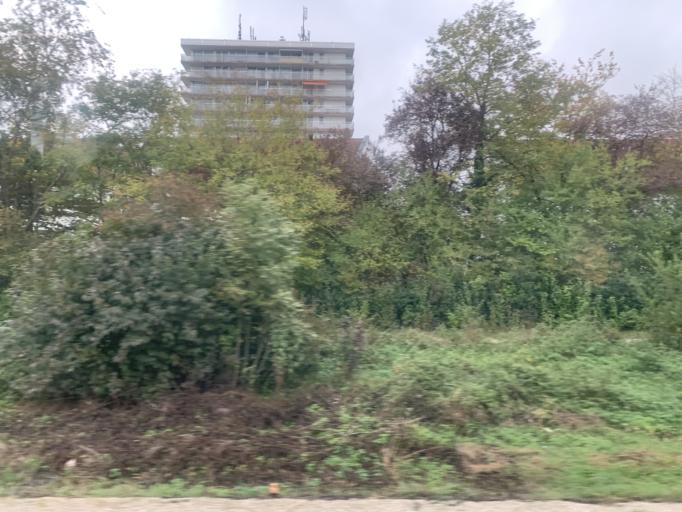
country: DE
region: Bavaria
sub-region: Upper Bavaria
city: Unterschleissheim
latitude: 48.2765
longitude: 11.5705
